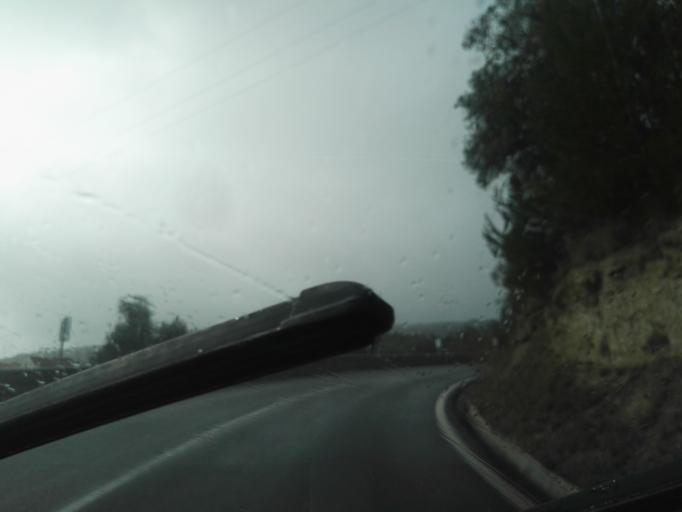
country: PT
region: Lisbon
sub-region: Vila Franca de Xira
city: Sobralinho
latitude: 38.9002
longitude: -9.0531
